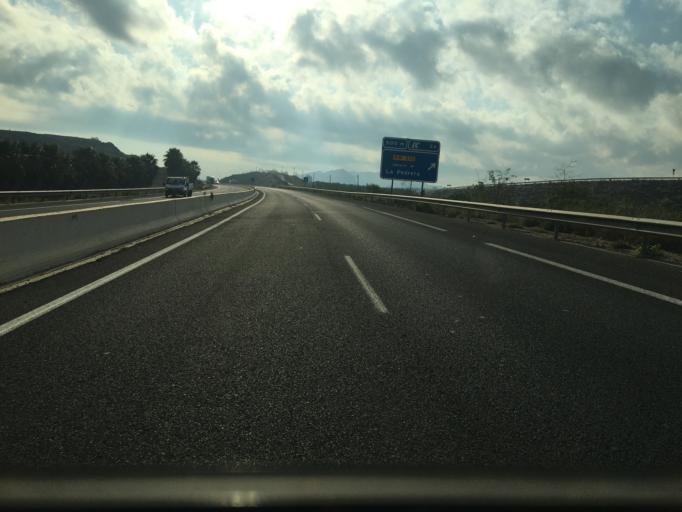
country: ES
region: Murcia
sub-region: Murcia
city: Beniel
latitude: 37.9952
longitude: -0.9969
